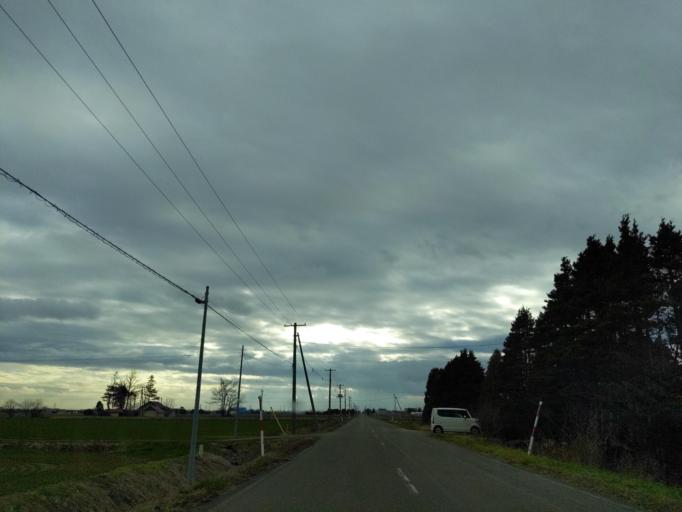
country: JP
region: Hokkaido
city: Kitahiroshima
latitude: 43.0367
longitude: 141.6877
